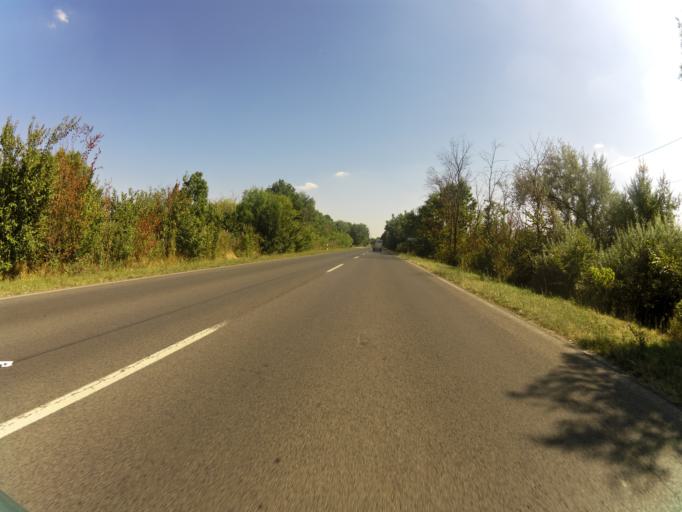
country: HU
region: Csongrad
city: Szatymaz
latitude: 46.3044
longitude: 20.0704
